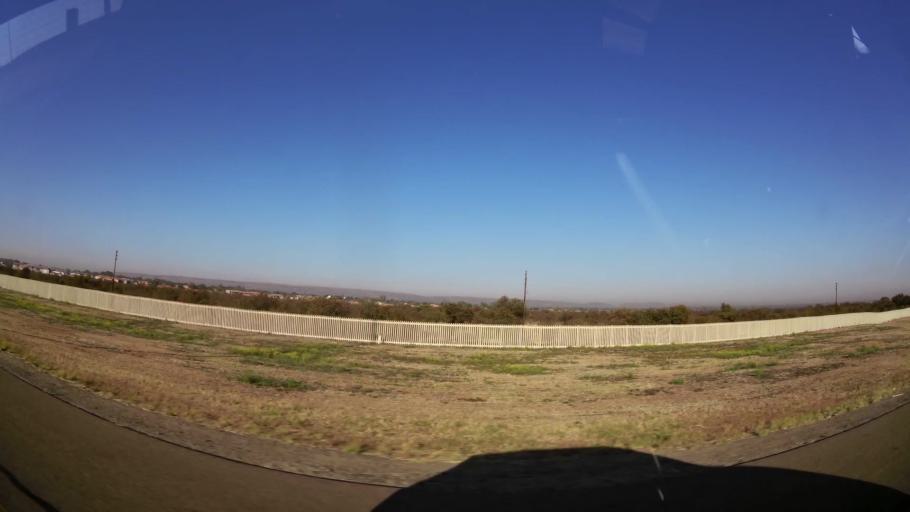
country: ZA
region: Gauteng
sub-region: City of Tshwane Metropolitan Municipality
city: Pretoria
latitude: -25.6458
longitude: 28.2715
